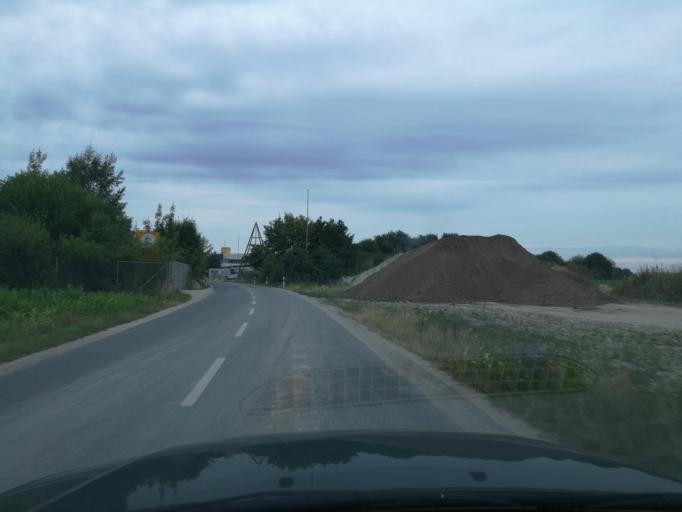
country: DE
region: Bavaria
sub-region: Regierungsbezirk Mittelfranken
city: Furth
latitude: 49.5139
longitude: 10.9978
